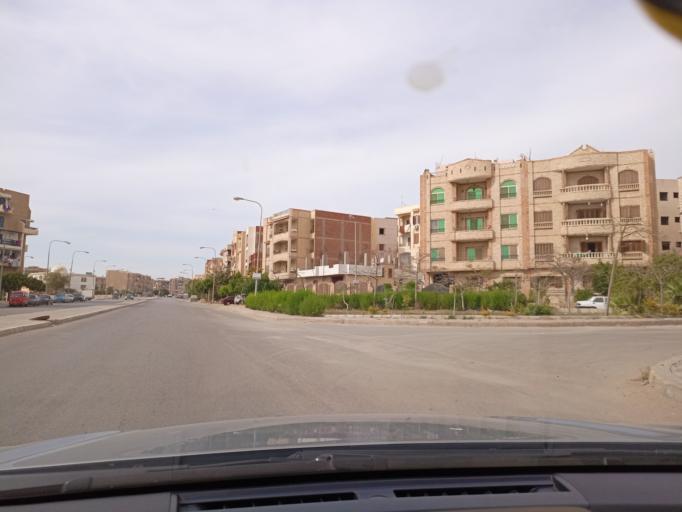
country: EG
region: Muhafazat al Qalyubiyah
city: Al Khankah
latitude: 30.2578
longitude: 31.4773
